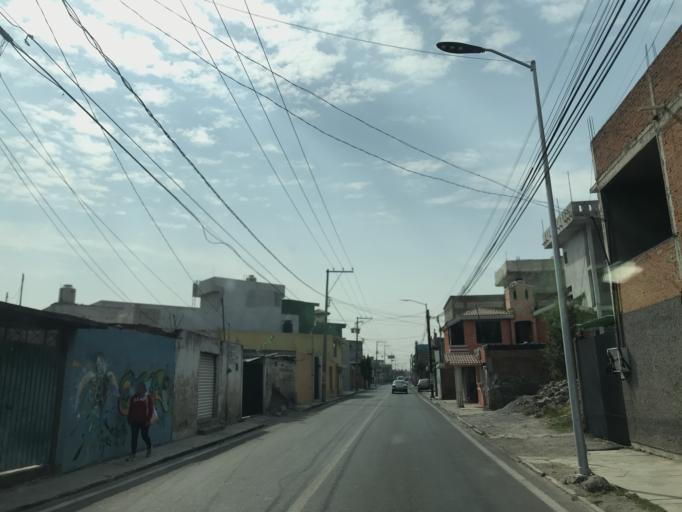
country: MX
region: Tlaxcala
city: Tenancingo
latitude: 19.1463
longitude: -98.1983
